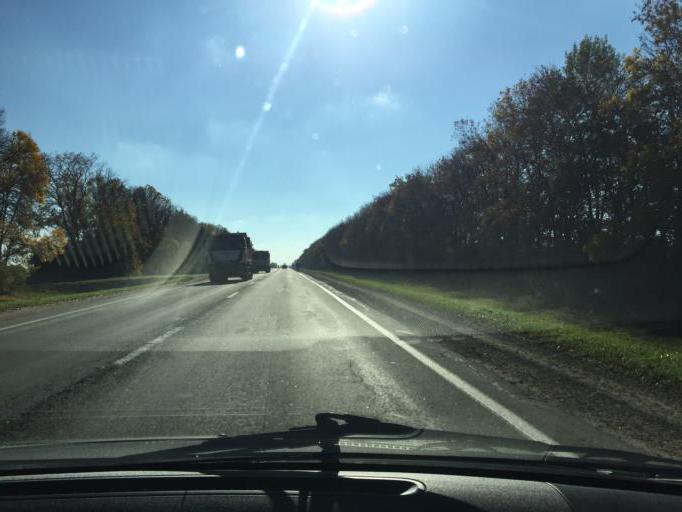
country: BY
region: Minsk
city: Slutsk
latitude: 52.9658
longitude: 27.4992
